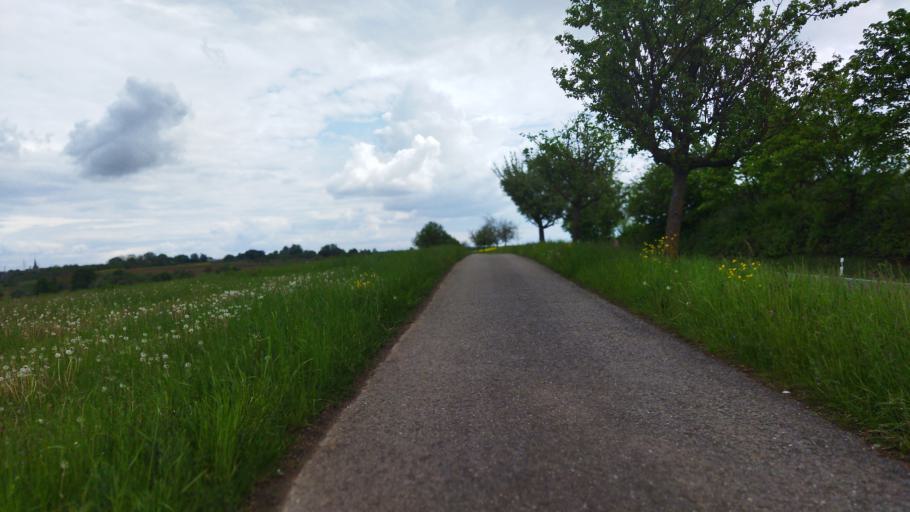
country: DE
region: Baden-Wuerttemberg
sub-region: Regierungsbezirk Stuttgart
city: Neckarwestheim
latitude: 49.0230
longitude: 9.1858
